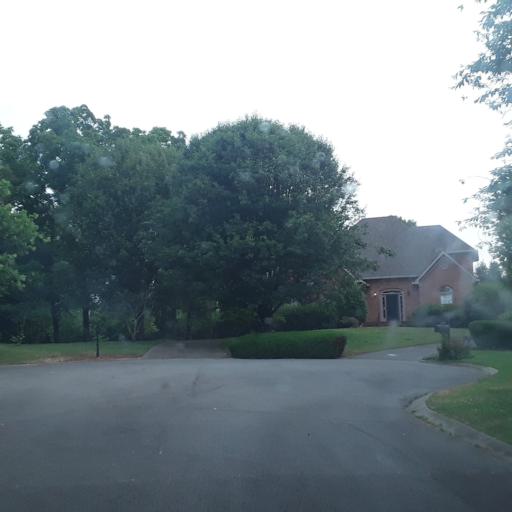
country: US
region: Tennessee
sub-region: Williamson County
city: Brentwood
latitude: 36.0473
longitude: -86.7724
